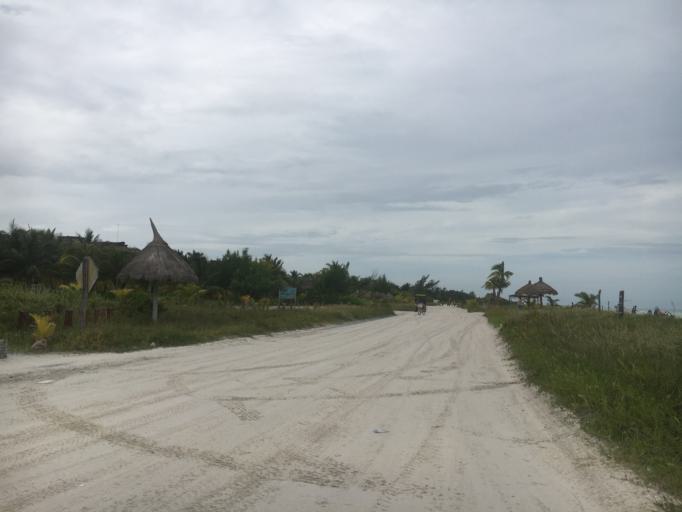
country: MX
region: Quintana Roo
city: Kantunilkin
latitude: 21.5296
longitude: -87.3718
